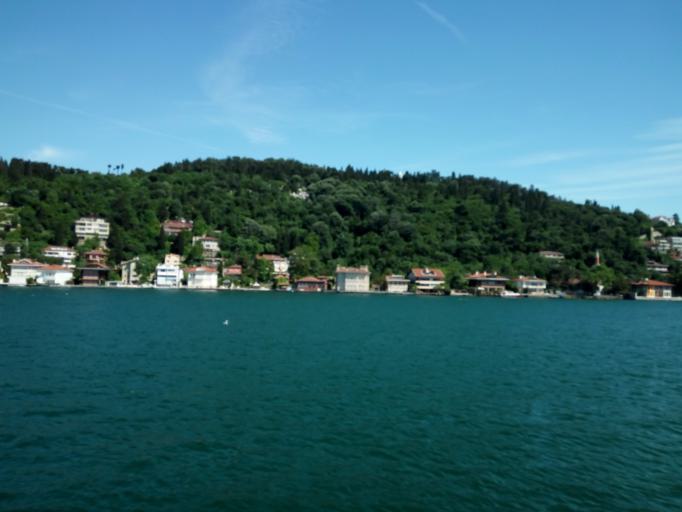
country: TR
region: Istanbul
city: UEskuedar
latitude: 41.0671
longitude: 29.0535
